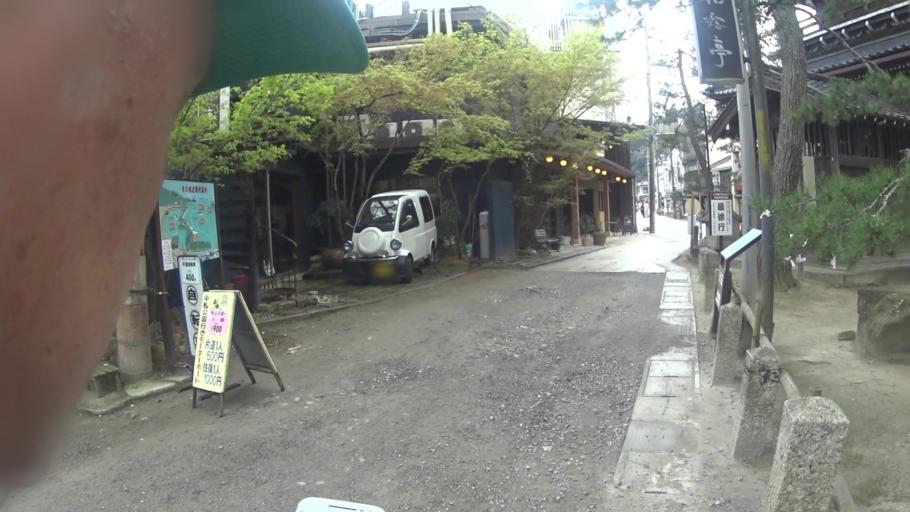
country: JP
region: Kyoto
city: Miyazu
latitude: 35.5581
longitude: 135.1847
